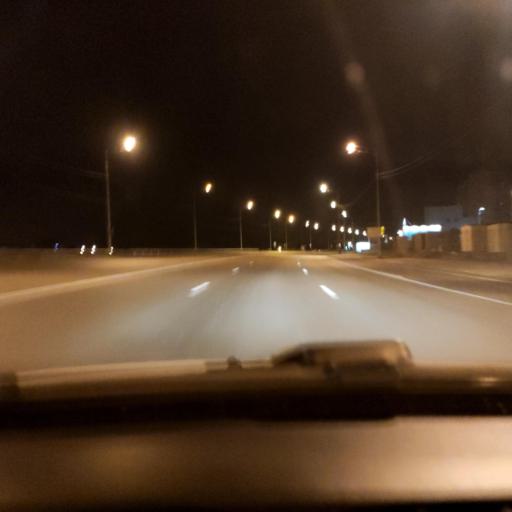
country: RU
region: Voronezj
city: Podgornoye
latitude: 51.7238
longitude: 39.1563
